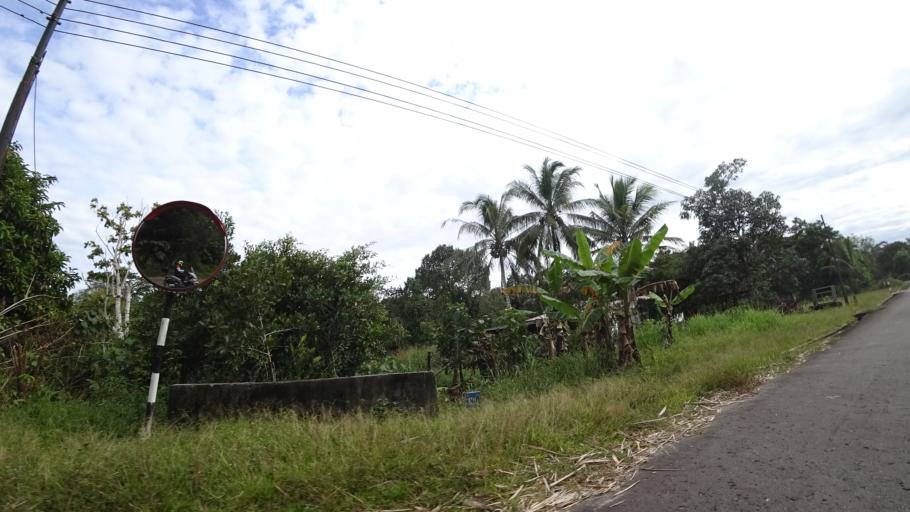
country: MY
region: Sarawak
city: Limbang
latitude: 4.8117
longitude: 114.9432
